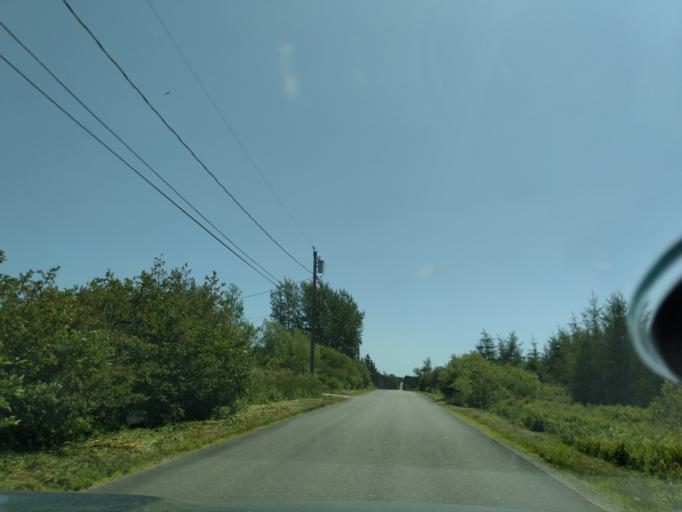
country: US
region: Maine
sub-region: Washington County
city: Eastport
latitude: 44.8400
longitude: -67.0144
